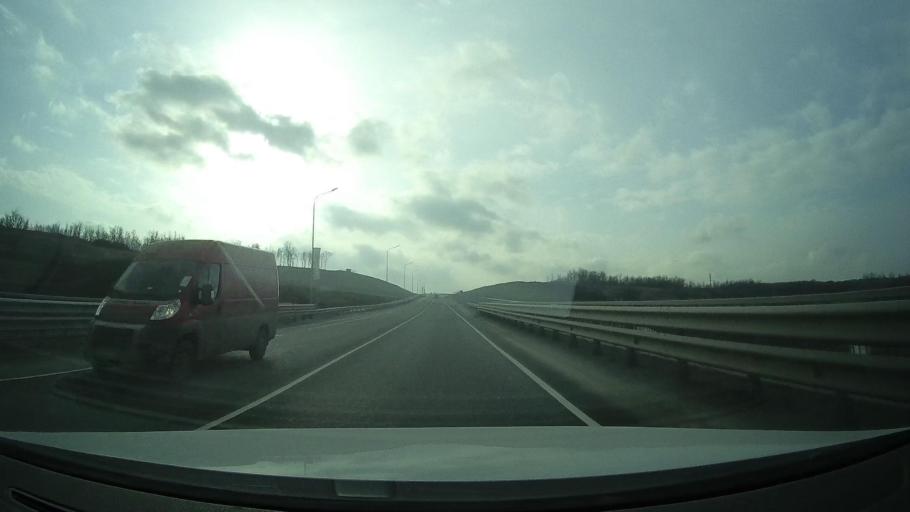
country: RU
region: Rostov
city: Grushevskaya
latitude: 47.4354
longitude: 39.8704
